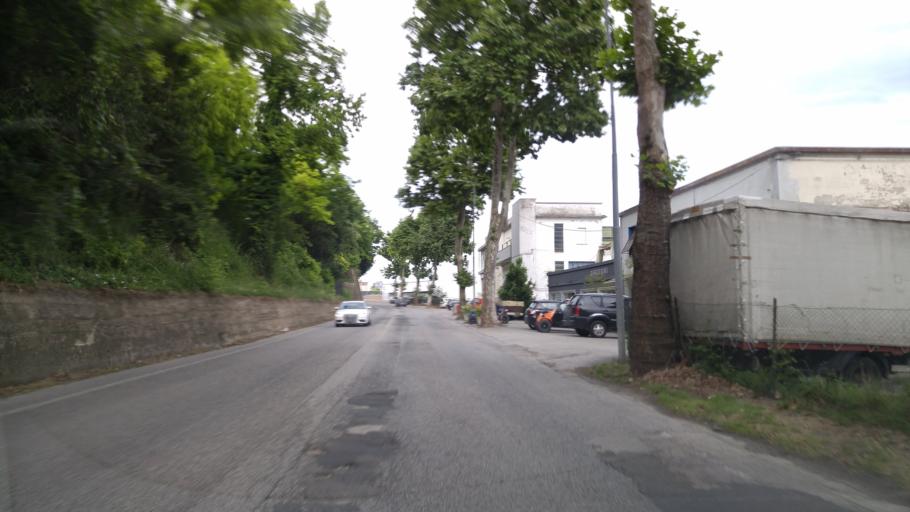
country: IT
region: The Marches
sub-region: Provincia di Pesaro e Urbino
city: Pesaro
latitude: 43.9082
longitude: 12.8657
